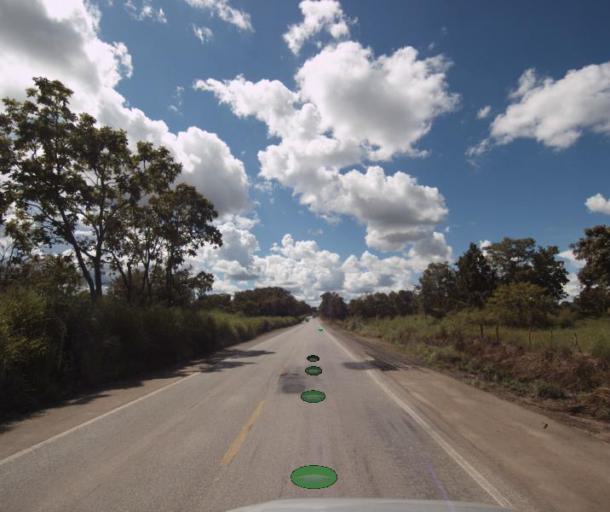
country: BR
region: Goias
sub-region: Porangatu
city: Porangatu
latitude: -13.6315
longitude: -49.0421
